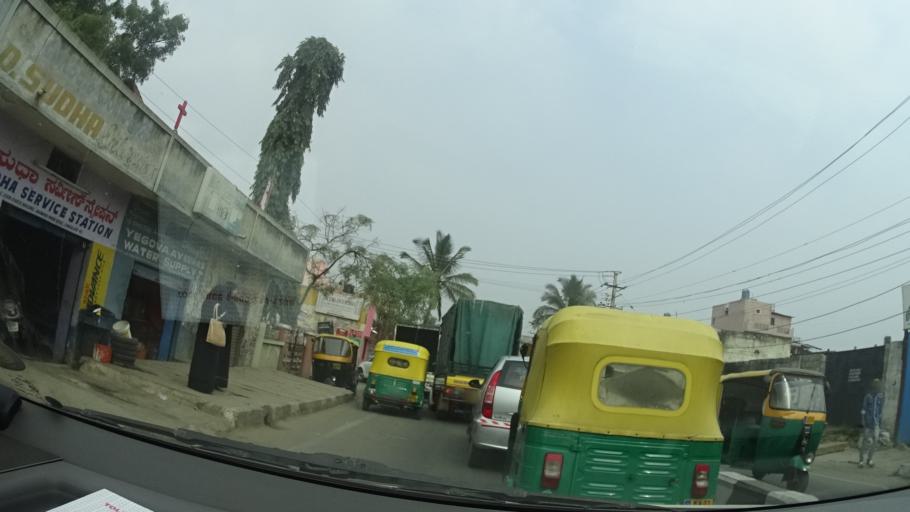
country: IN
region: Karnataka
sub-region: Bangalore Urban
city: Bangalore
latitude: 13.0282
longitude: 77.6206
